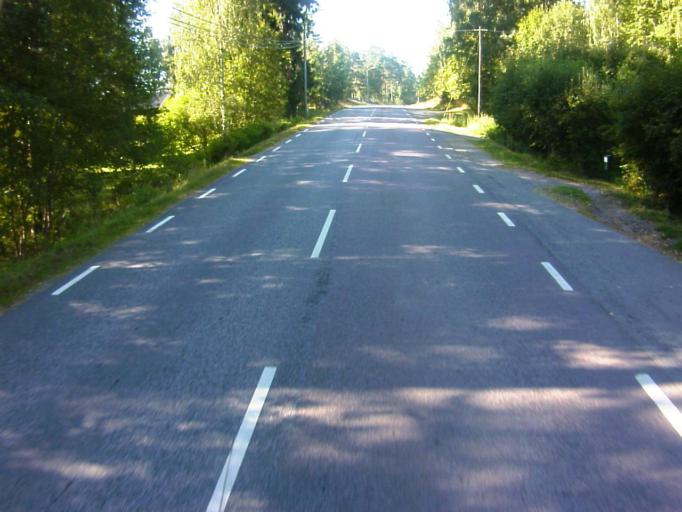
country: SE
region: Soedermanland
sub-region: Eskilstuna Kommun
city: Skogstorp
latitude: 59.3354
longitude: 16.4312
